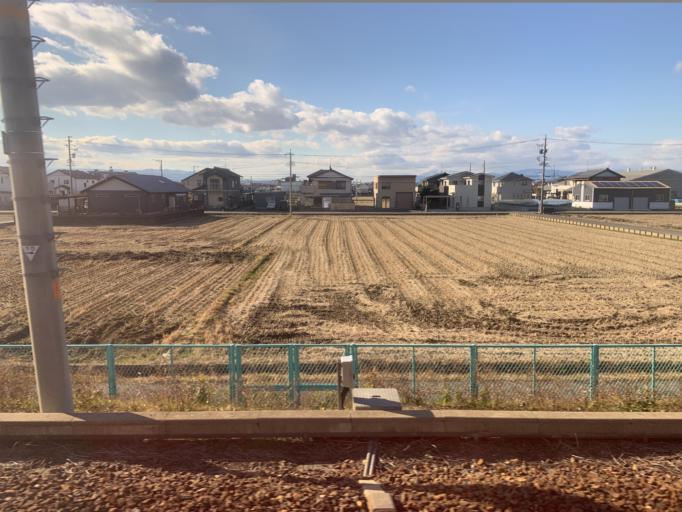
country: JP
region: Aichi
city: Kuroda
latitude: 35.3595
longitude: 136.7792
